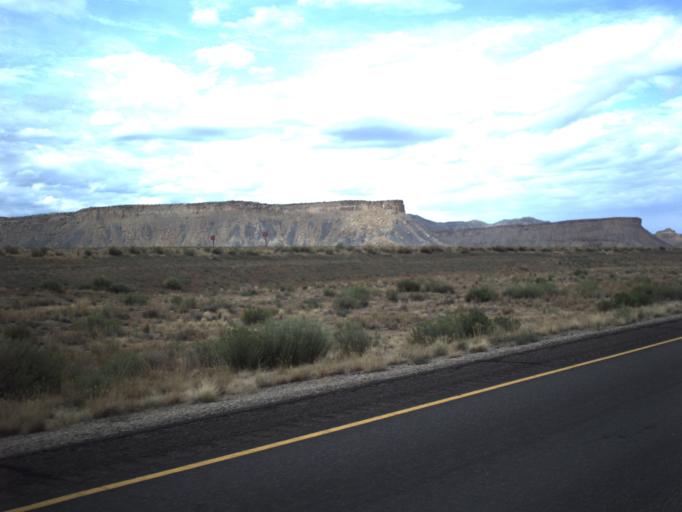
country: US
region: Utah
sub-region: Grand County
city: Moab
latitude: 38.9550
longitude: -109.7526
